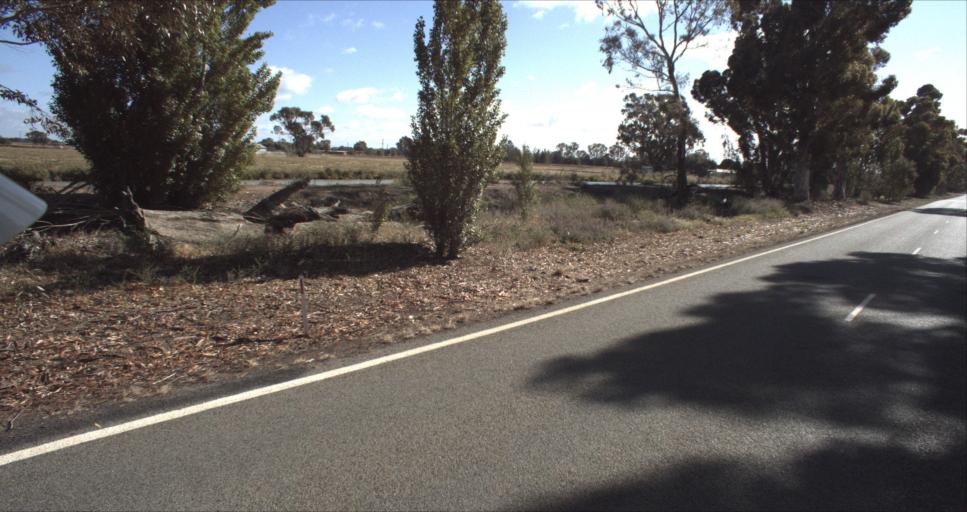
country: AU
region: New South Wales
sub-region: Leeton
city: Leeton
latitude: -34.5465
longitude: 146.3257
